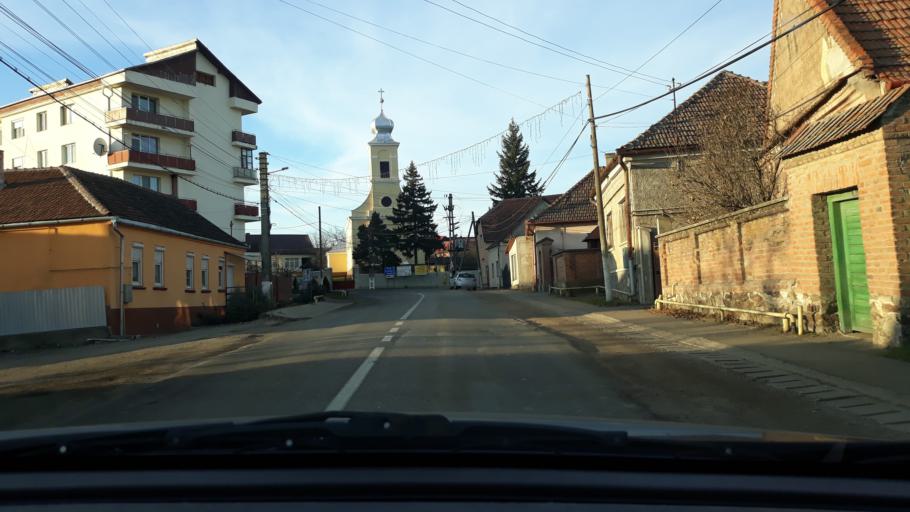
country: RO
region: Bihor
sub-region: Comuna Suplacu de Barcau
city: Suplacu de Barcau
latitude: 47.2584
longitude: 22.5269
